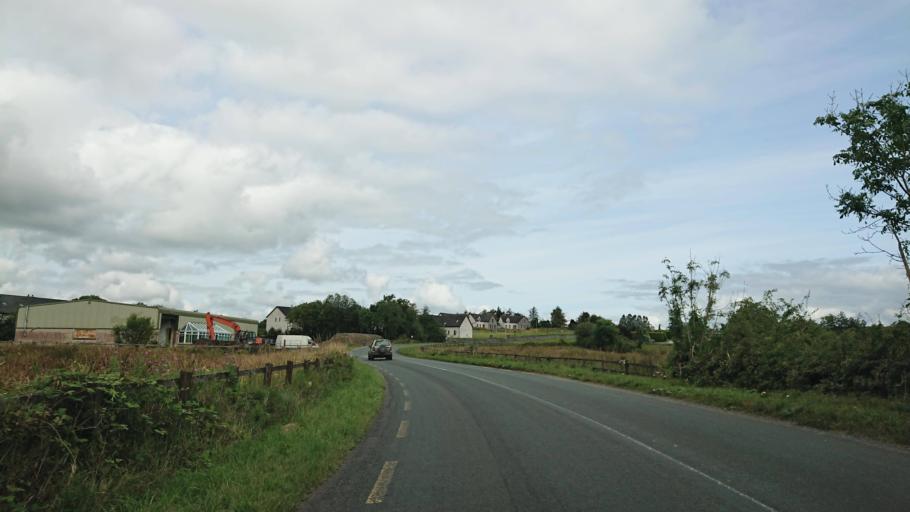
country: IE
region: Connaught
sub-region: County Leitrim
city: Carrick-on-Shannon
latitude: 54.0521
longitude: -8.0388
